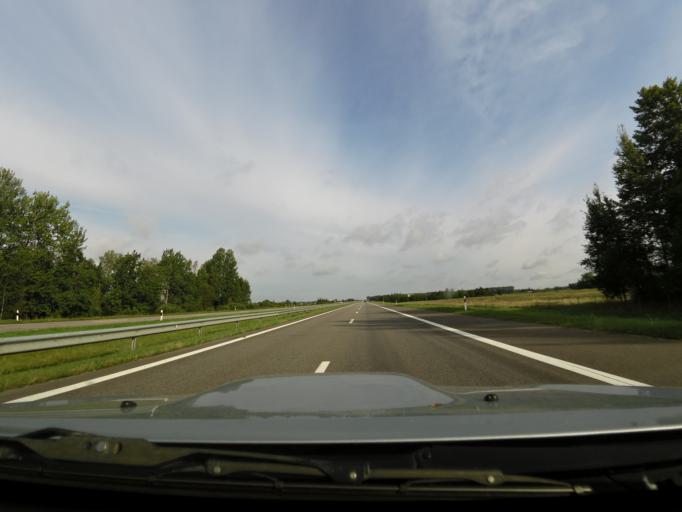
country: LT
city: Sirvintos
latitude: 55.0531
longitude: 24.8920
